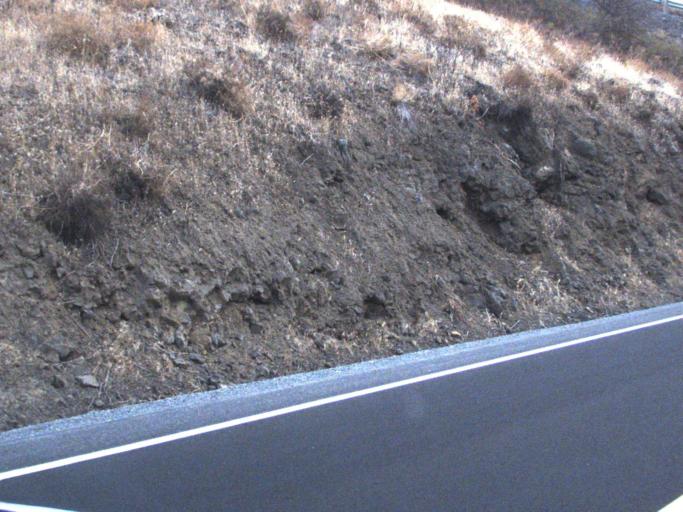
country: US
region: Washington
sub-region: Okanogan County
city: Coulee Dam
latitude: 47.8628
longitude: -118.7264
